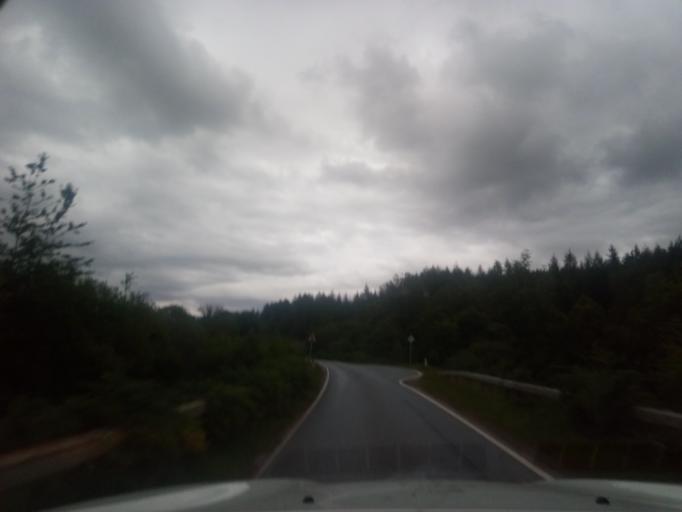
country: GB
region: Scotland
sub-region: Highland
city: Fort William
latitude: 56.8555
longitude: -5.3451
